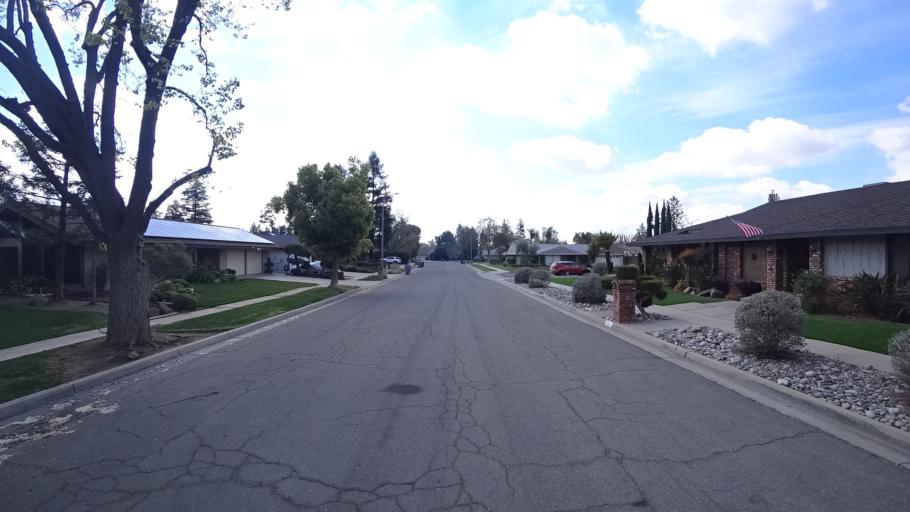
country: US
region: California
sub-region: Fresno County
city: Fresno
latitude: 36.8341
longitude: -119.8505
